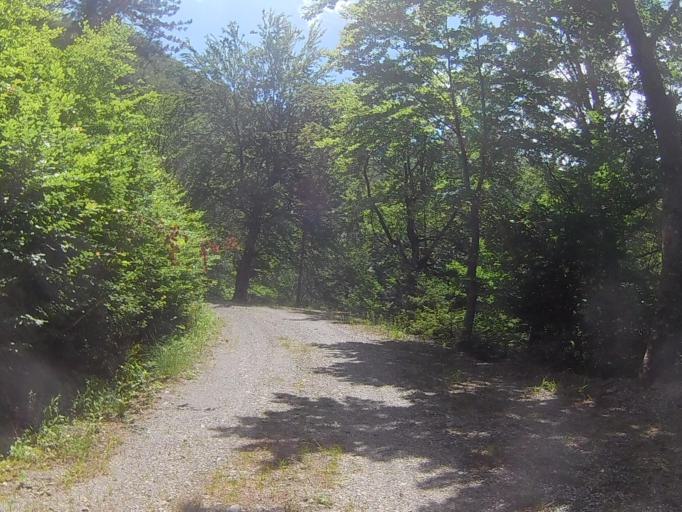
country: SI
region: Selnica ob Dravi
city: Selnica ob Dravi
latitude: 46.5222
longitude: 15.4892
